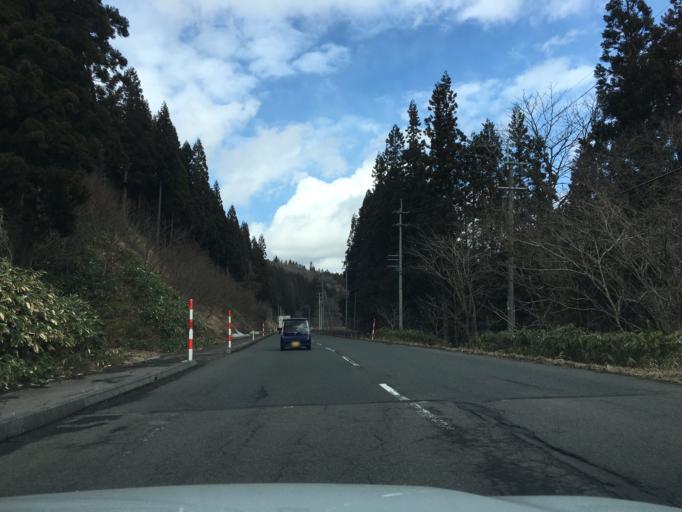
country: JP
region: Akita
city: Takanosu
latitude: 40.0947
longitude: 140.3410
